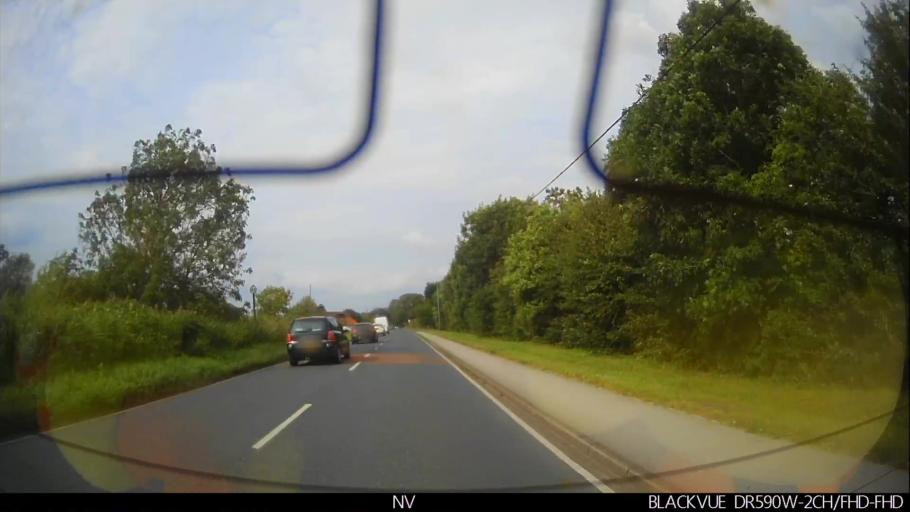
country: GB
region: England
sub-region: City of York
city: Huntington
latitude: 54.0176
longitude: -1.0474
